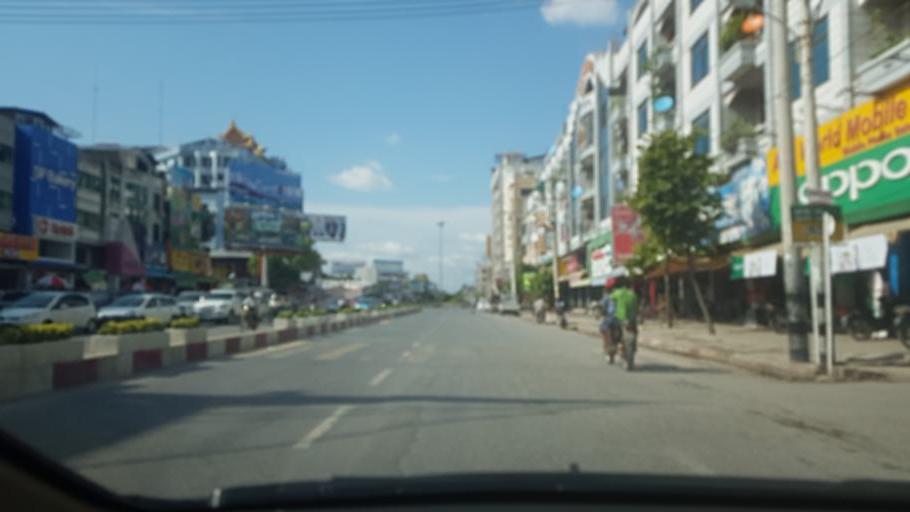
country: MM
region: Mandalay
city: Mandalay
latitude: 21.9752
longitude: 96.0869
